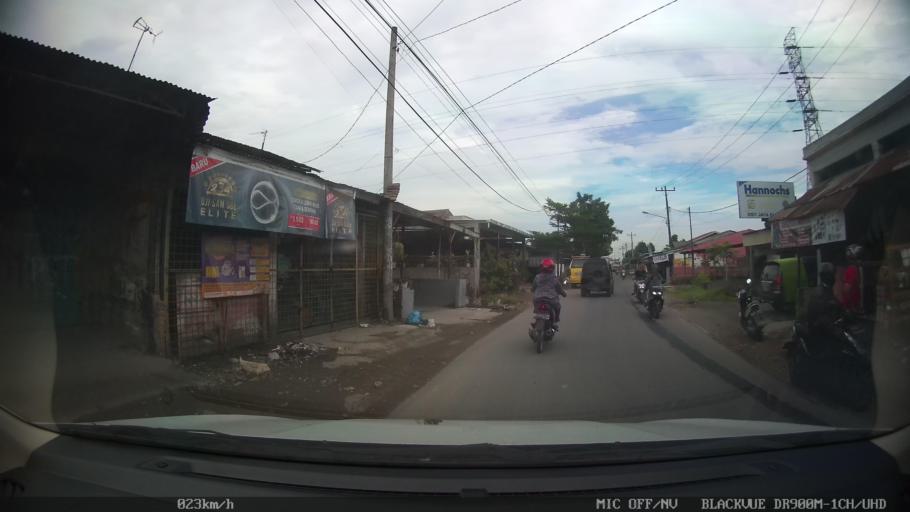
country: ID
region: North Sumatra
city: Sunggal
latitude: 3.6188
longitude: 98.6019
